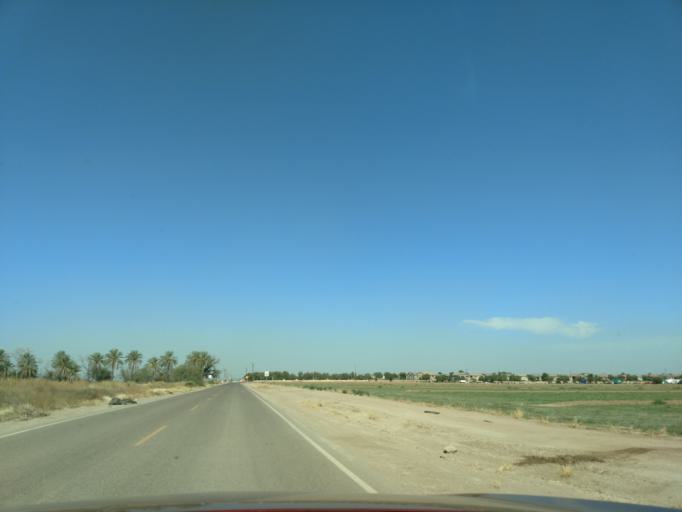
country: US
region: Arizona
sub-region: Maricopa County
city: Laveen
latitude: 33.3593
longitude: -112.1863
